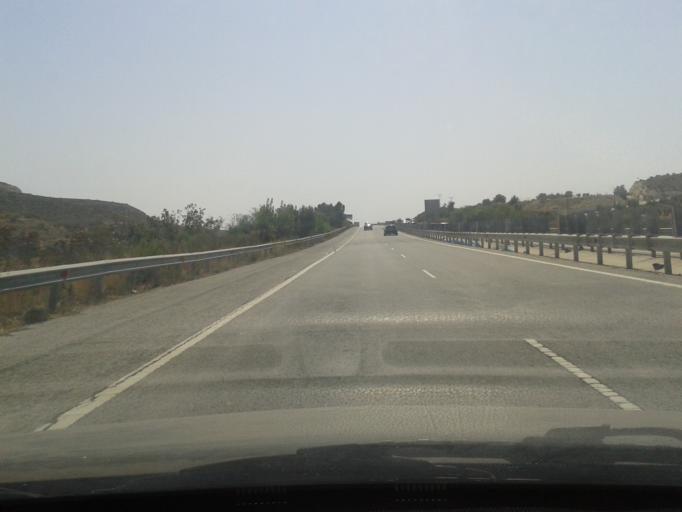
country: CY
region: Larnaka
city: Kofinou
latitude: 34.7879
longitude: 33.3440
